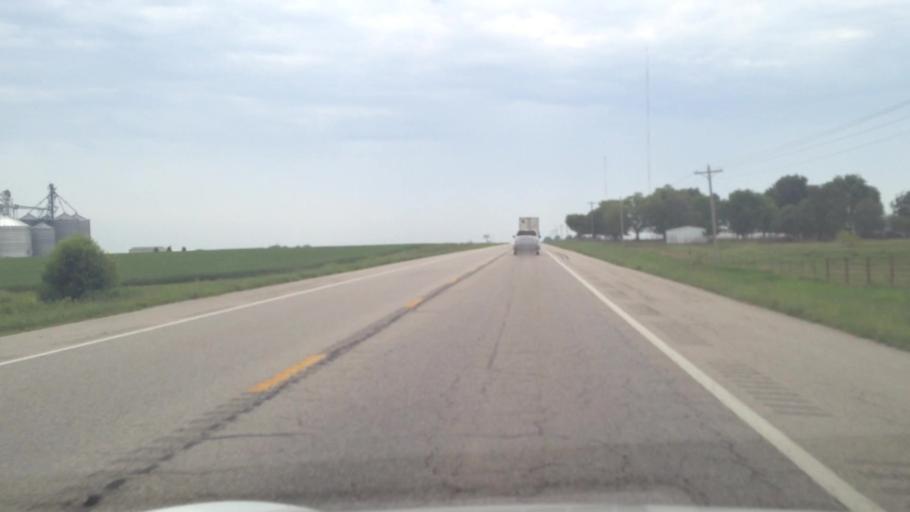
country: US
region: Missouri
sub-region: Jasper County
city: Carl Junction
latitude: 37.2359
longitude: -94.7050
